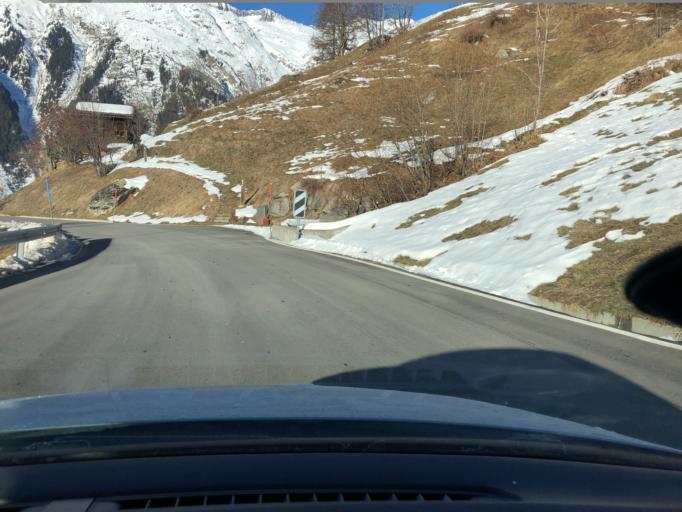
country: CH
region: Valais
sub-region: Goms District
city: Fiesch
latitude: 46.4307
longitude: 8.1534
